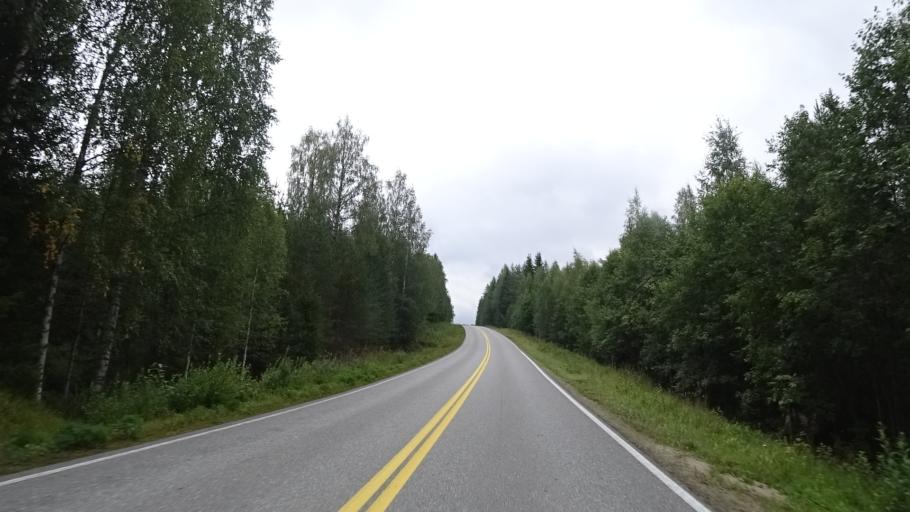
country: FI
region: North Karelia
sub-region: Pielisen Karjala
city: Lieksa
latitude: 63.2815
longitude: 30.5657
